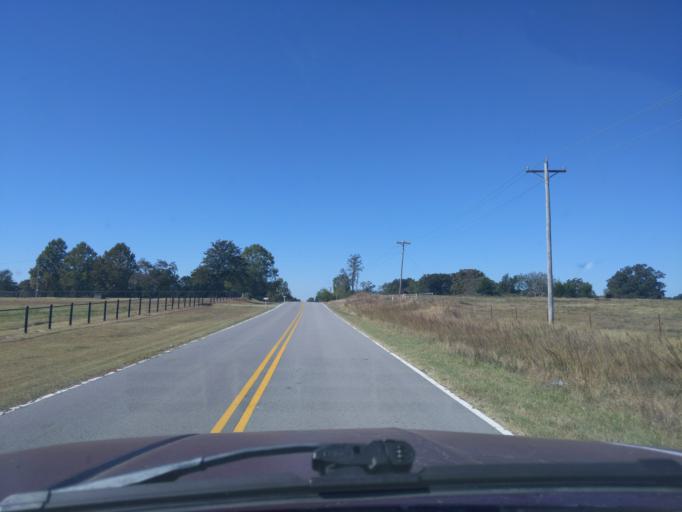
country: US
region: Oklahoma
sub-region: Creek County
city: Bristow
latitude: 35.7120
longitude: -96.4015
